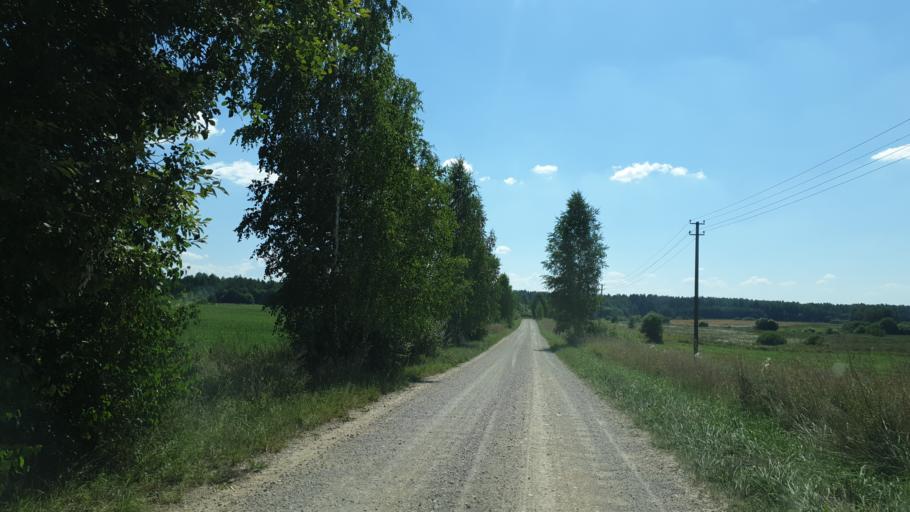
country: LT
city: Sirvintos
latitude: 54.9071
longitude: 24.9112
